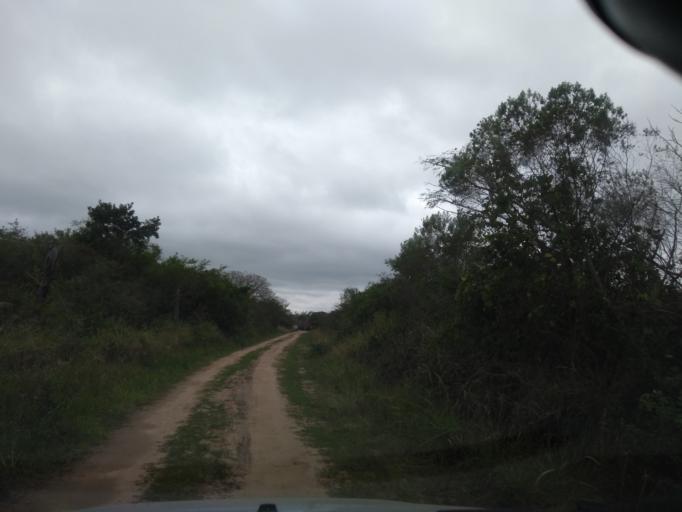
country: AR
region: Chaco
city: Barranqueras
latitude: -27.4314
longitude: -58.9280
